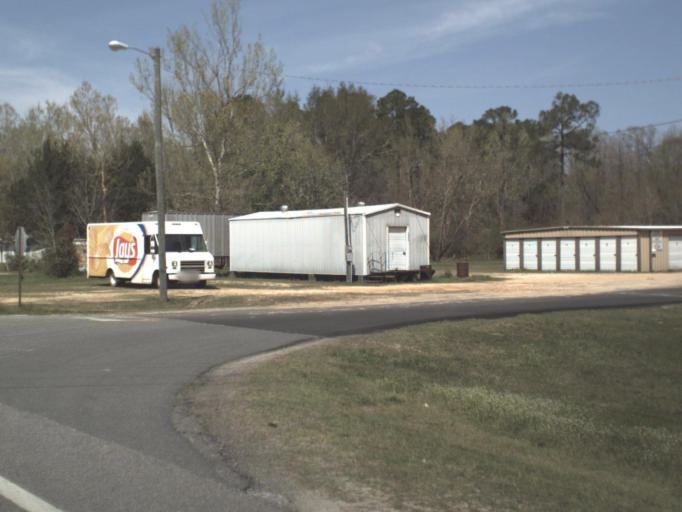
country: US
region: Florida
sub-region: Holmes County
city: Bonifay
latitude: 30.7887
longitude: -85.6905
